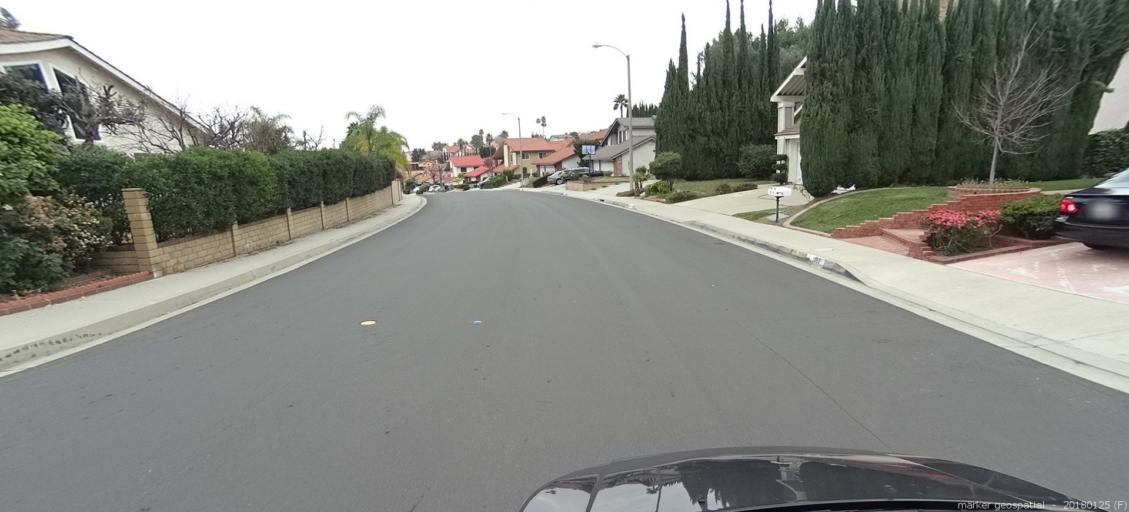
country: US
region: California
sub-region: Los Angeles County
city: Walnut
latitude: 33.9646
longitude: -117.8384
